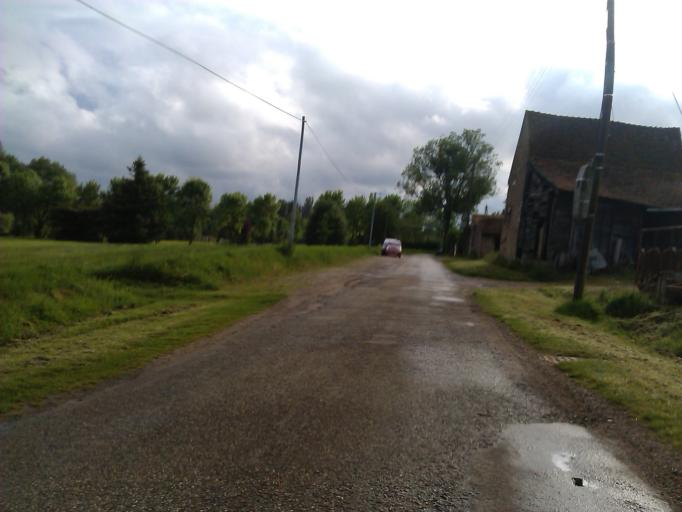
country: FR
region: Bourgogne
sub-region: Departement de Saone-et-Loire
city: Crissey
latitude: 46.8151
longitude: 4.8908
